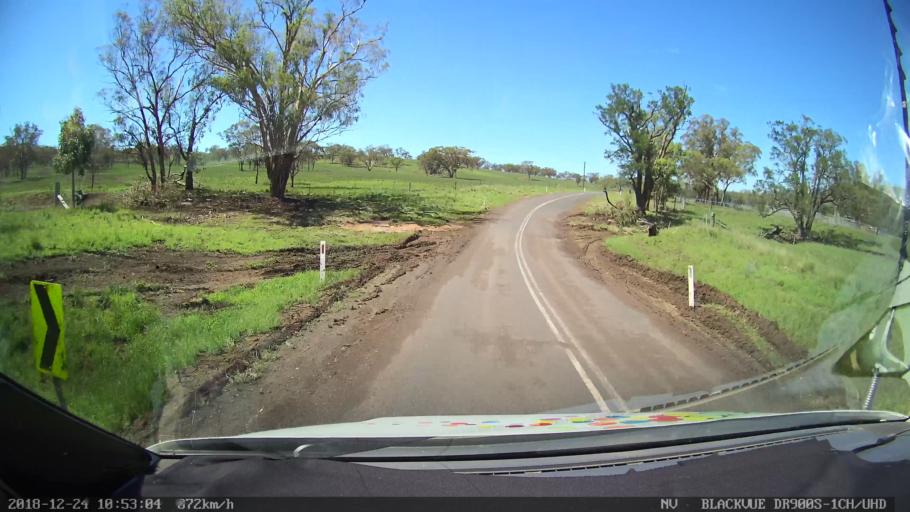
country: AU
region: New South Wales
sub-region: Upper Hunter Shire
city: Merriwa
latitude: -31.9880
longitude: 150.4229
